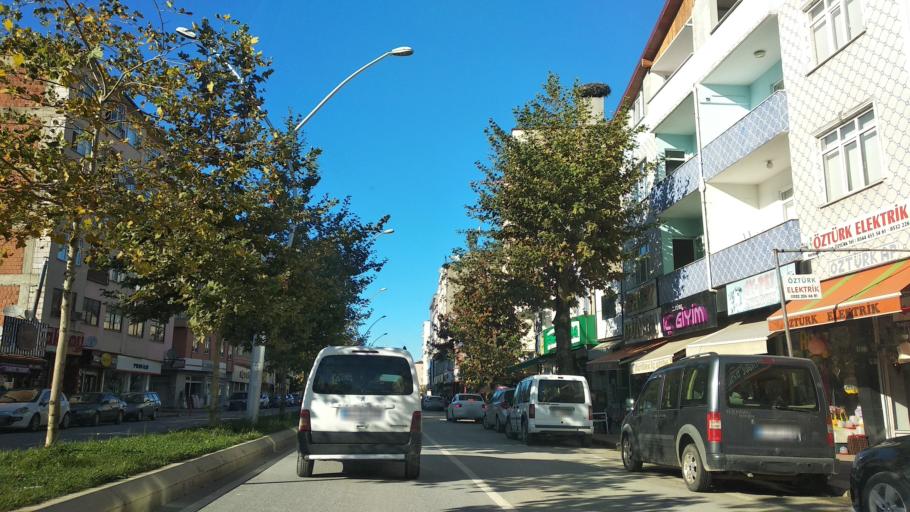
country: TR
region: Sakarya
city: Karasu
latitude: 41.0976
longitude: 30.6925
